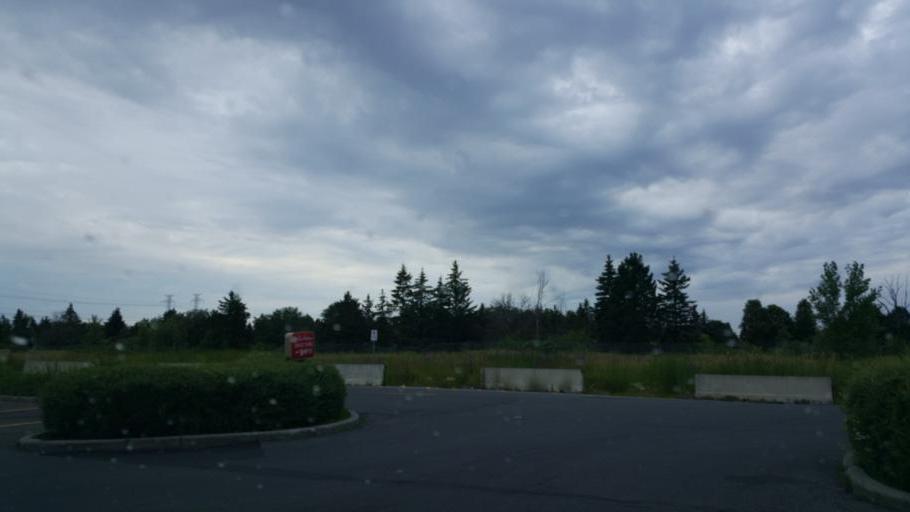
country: CA
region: Ontario
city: Ottawa
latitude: 45.3824
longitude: -75.6316
